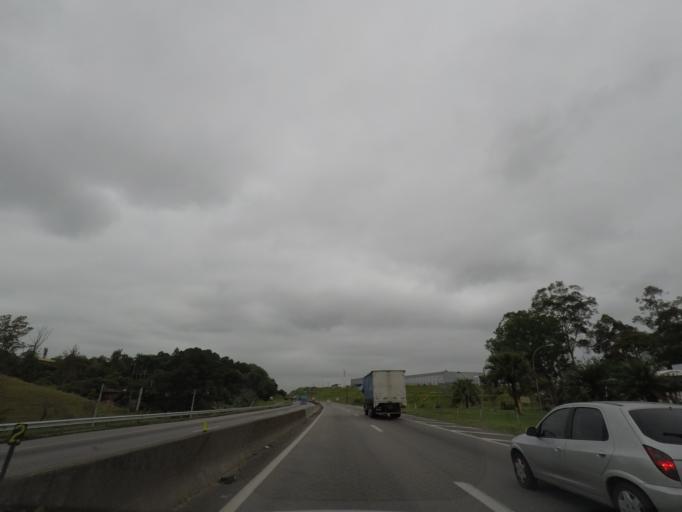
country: BR
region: Sao Paulo
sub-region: Jacarei
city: Jacarei
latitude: -23.3004
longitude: -46.0165
